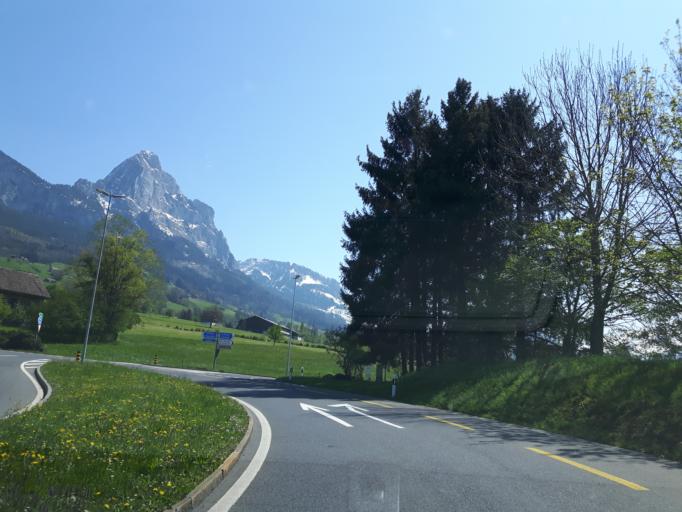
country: CH
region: Schwyz
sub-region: Bezirk Schwyz
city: Schwyz
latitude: 47.0303
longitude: 8.6431
